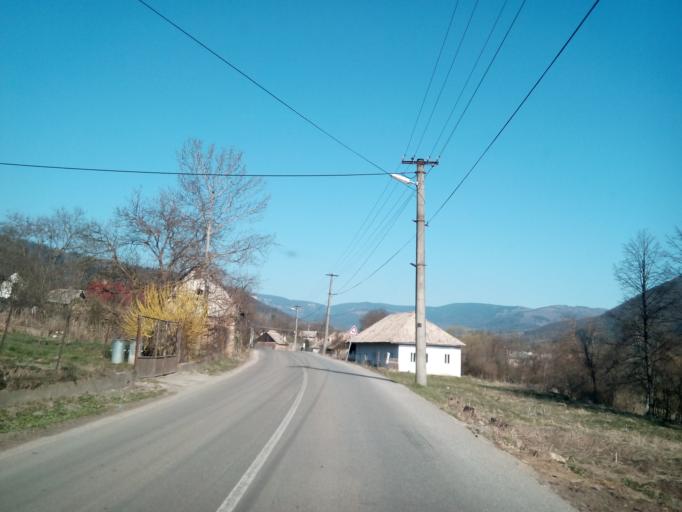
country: SK
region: Kosicky
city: Dobsina
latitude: 48.6833
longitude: 20.3305
